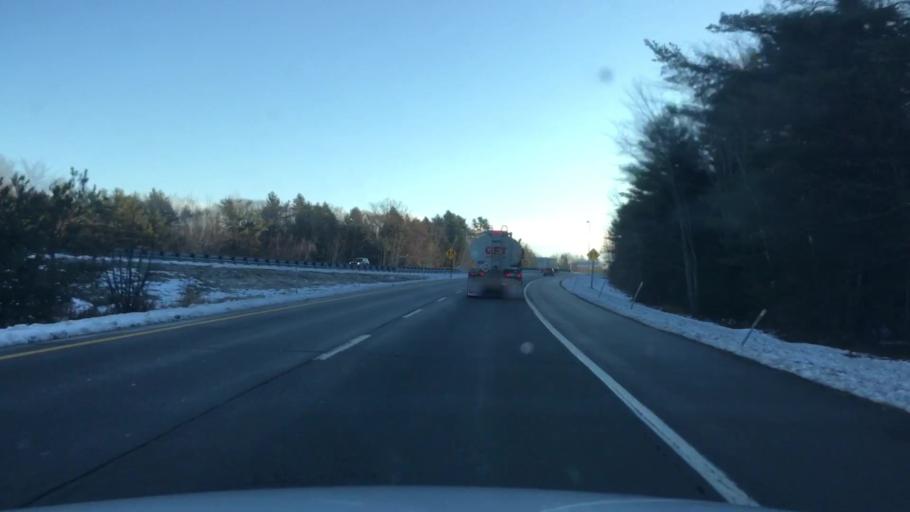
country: US
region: Maine
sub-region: Sagadahoc County
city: Topsham
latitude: 43.9171
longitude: -70.0188
